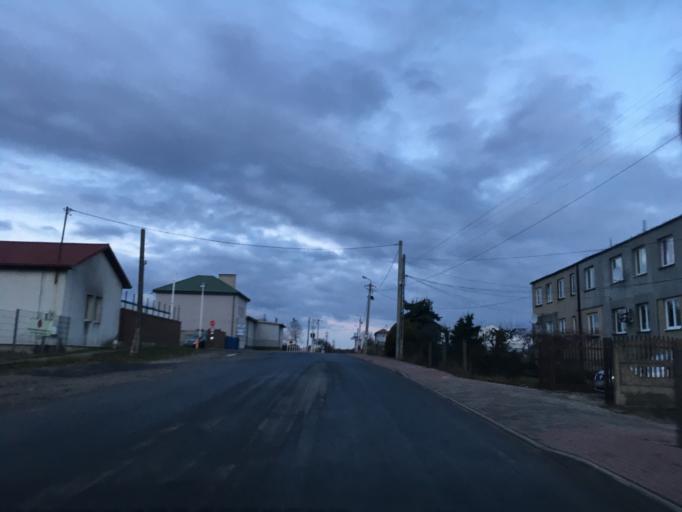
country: PL
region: Masovian Voivodeship
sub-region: Powiat pruszkowski
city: Owczarnia
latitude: 52.0809
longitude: 20.7226
